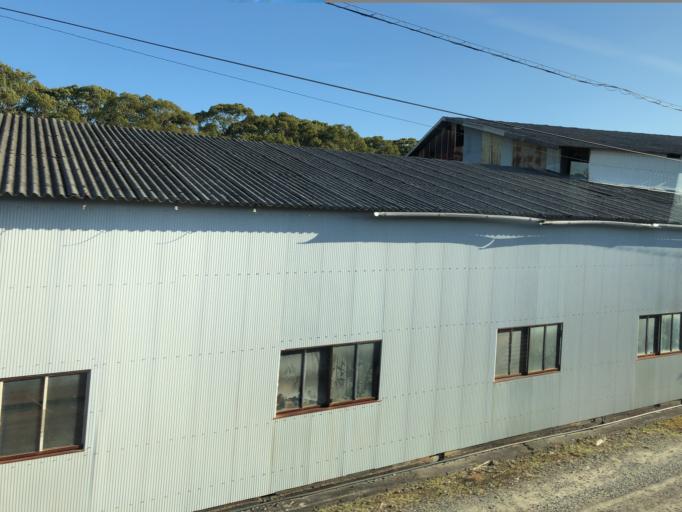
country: JP
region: Kochi
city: Nakamura
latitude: 33.0292
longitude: 133.0157
